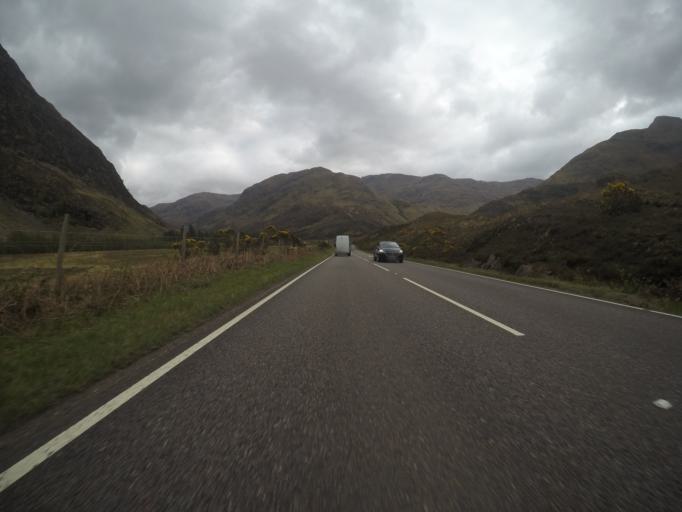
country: GB
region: Scotland
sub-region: Highland
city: Fort William
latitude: 57.1740
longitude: -5.3620
